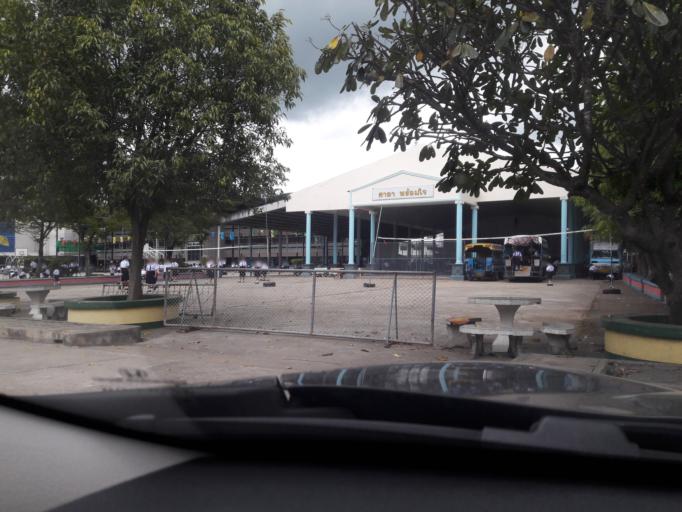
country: TH
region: Ratchaburi
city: Damnoen Saduak
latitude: 13.5910
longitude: 99.9407
